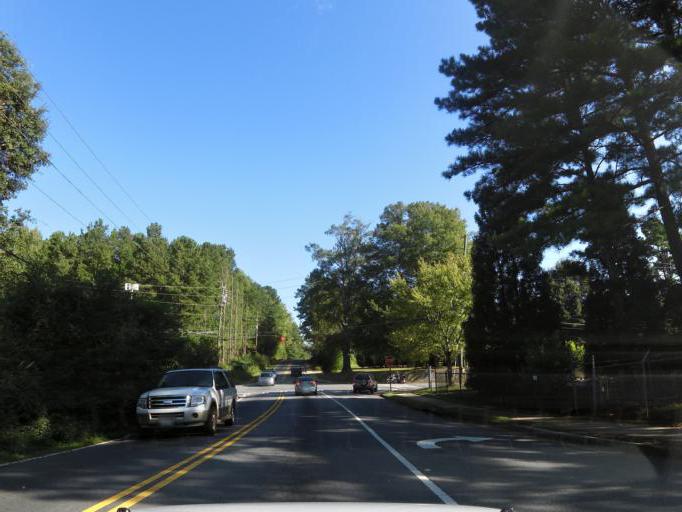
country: US
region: Georgia
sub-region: Cobb County
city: Acworth
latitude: 34.0152
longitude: -84.6755
